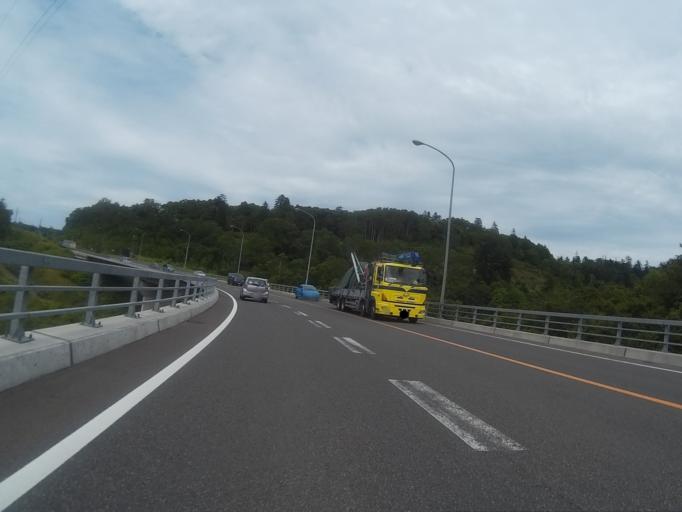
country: JP
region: Hokkaido
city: Sapporo
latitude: 42.8500
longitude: 141.0898
